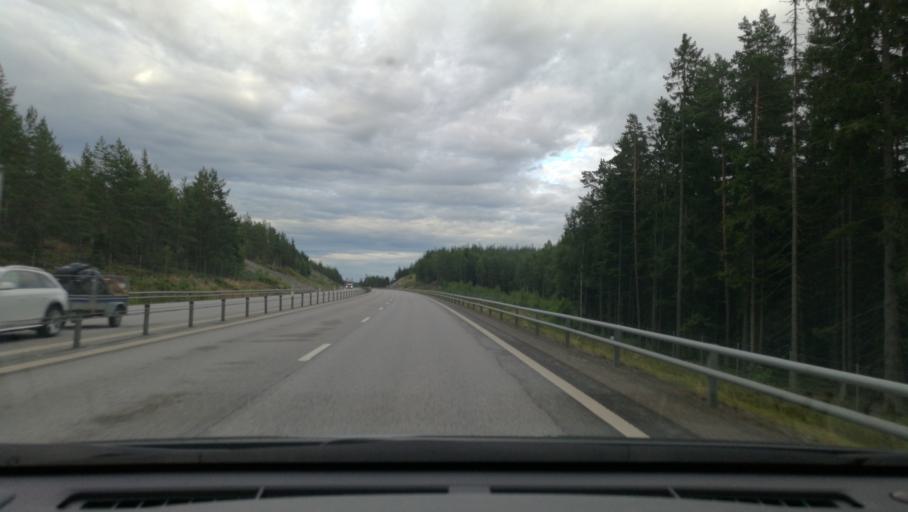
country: SE
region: OEstergoetland
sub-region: Norrkopings Kommun
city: Svartinge
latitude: 58.6646
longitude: 16.0205
